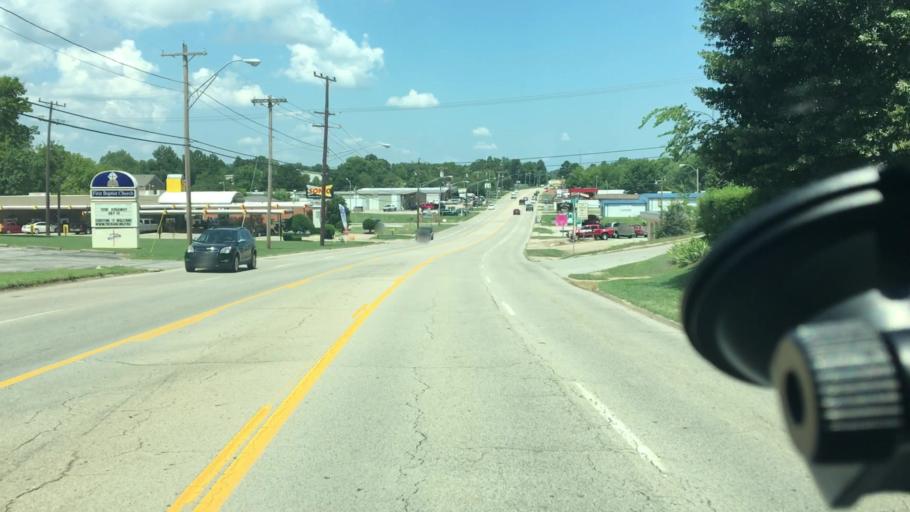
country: US
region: Arkansas
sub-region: Sebastian County
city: Barling
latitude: 35.3257
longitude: -94.3021
